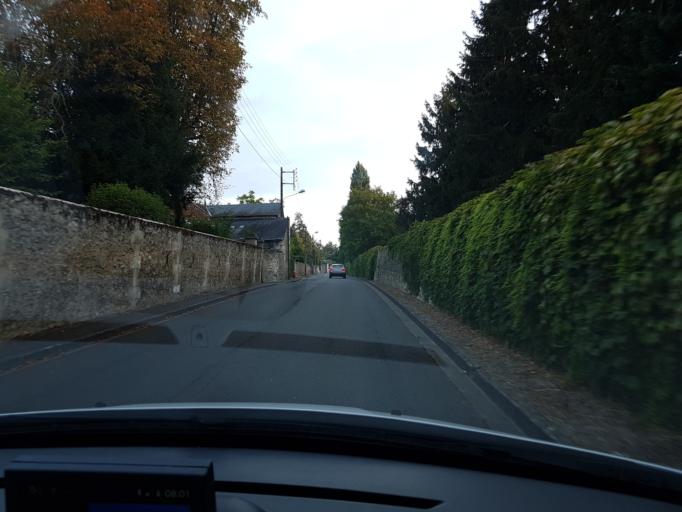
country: FR
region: Centre
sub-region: Departement d'Indre-et-Loire
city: Saint-Avertin
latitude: 47.3612
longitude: 0.7293
